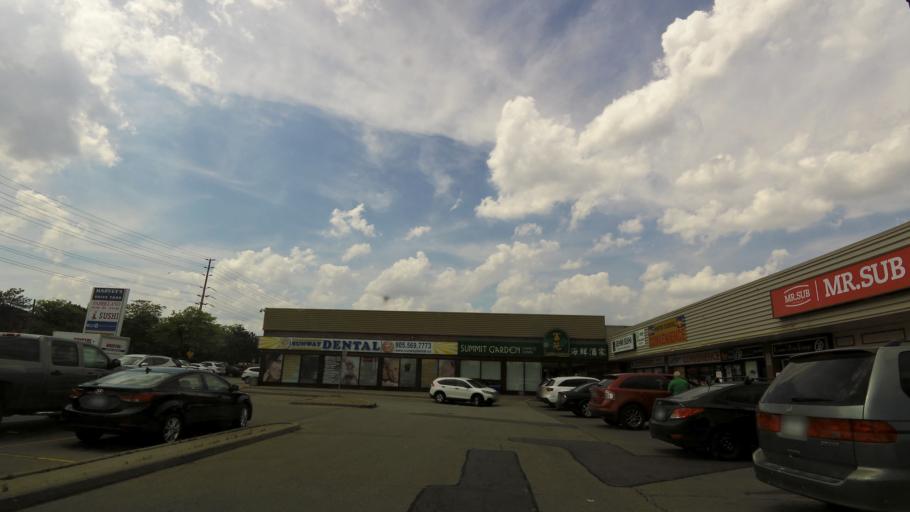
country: CA
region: Ontario
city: Mississauga
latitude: 43.5237
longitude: -79.6819
